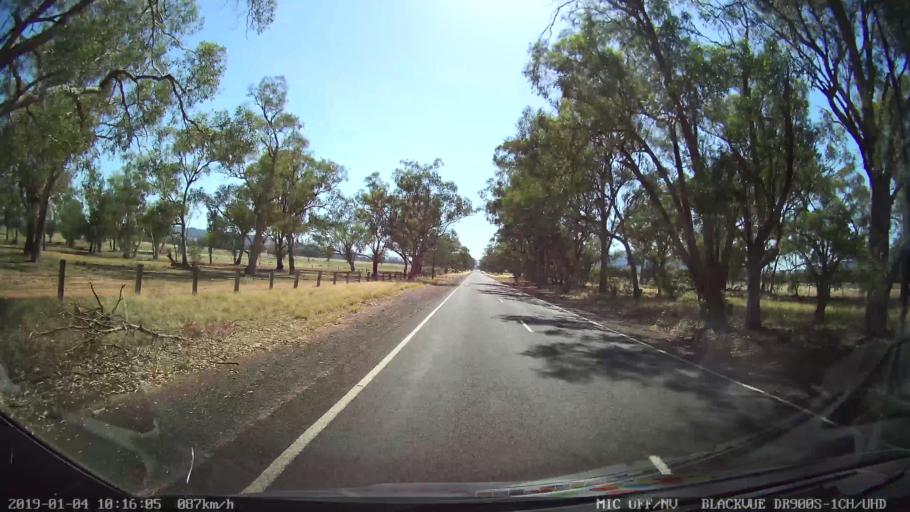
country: AU
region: New South Wales
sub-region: Cabonne
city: Canowindra
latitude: -33.3860
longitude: 148.4313
